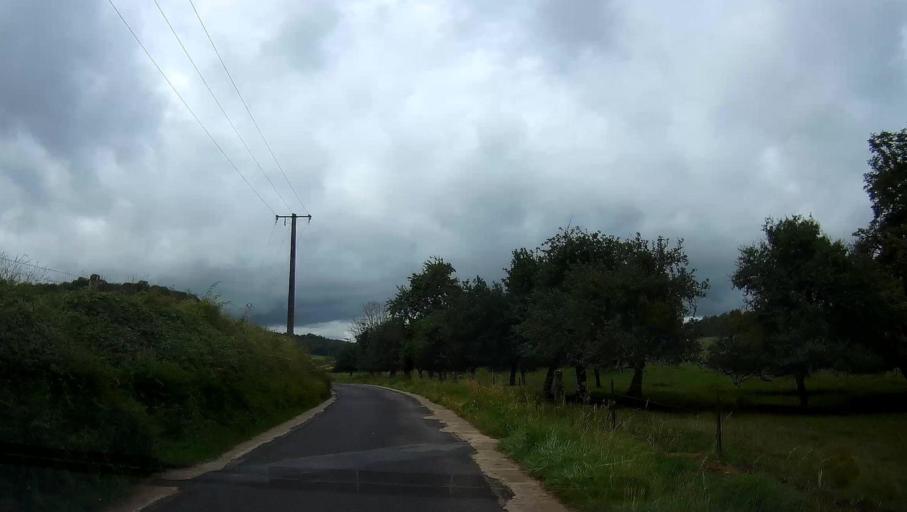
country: FR
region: Champagne-Ardenne
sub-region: Departement des Ardennes
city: Rimogne
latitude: 49.7680
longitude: 4.4873
